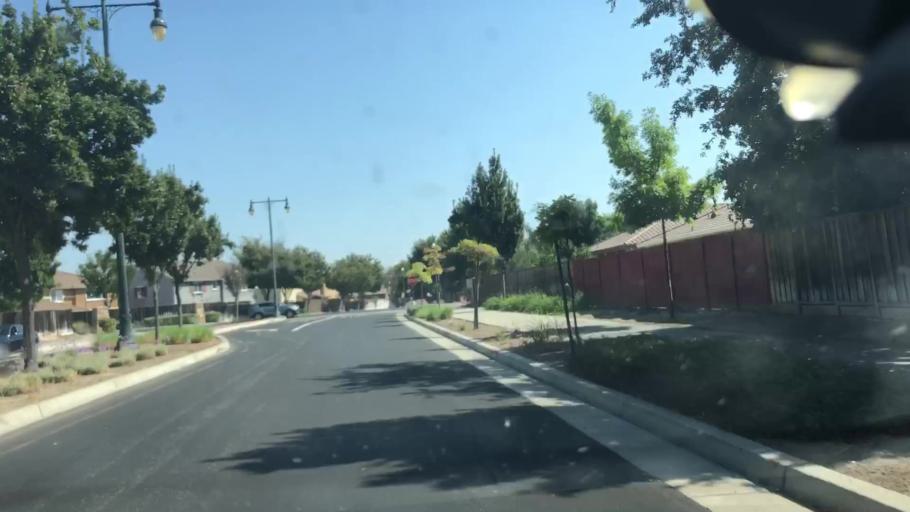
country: US
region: California
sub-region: San Joaquin County
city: Lathrop
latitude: 37.8090
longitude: -121.3051
